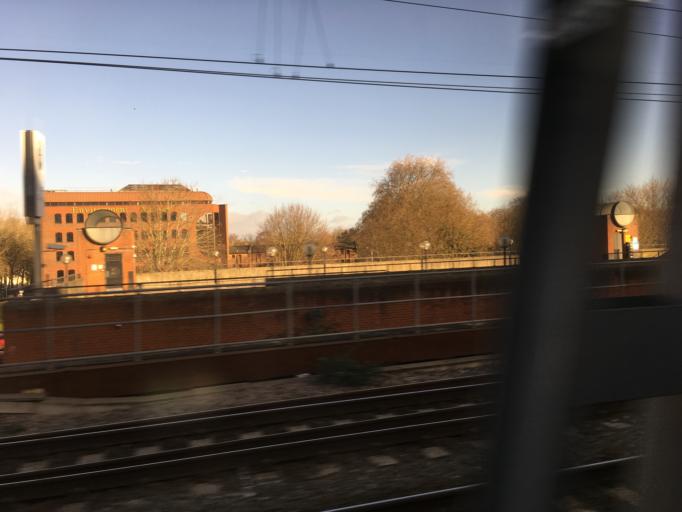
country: GB
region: England
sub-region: Reading
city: Reading
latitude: 51.4590
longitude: -0.9676
